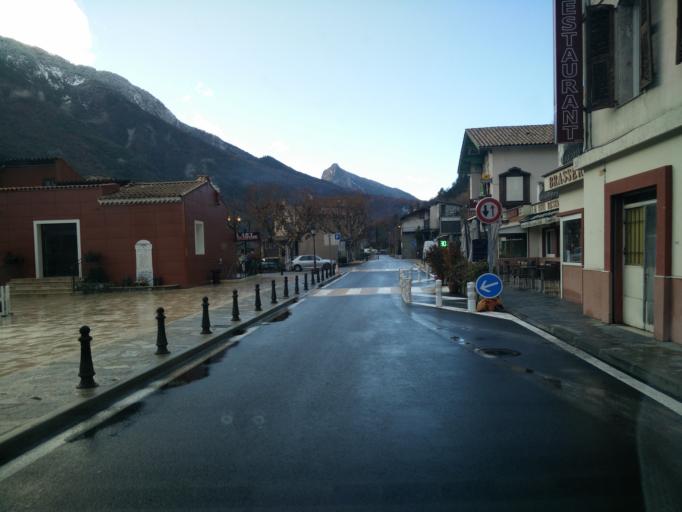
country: FR
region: Provence-Alpes-Cote d'Azur
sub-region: Departement des Alpes-Maritimes
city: Puget-Theniers
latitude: 43.9478
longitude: 7.0072
